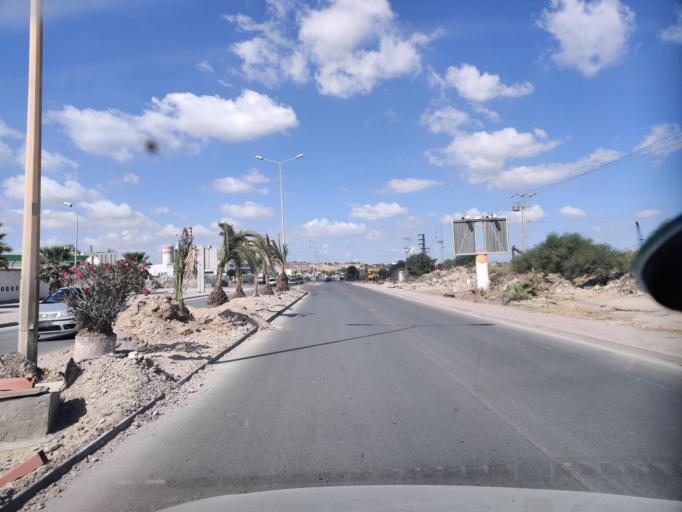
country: TN
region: Bin 'Arus
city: Ben Arous
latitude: 36.7765
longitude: 10.2113
